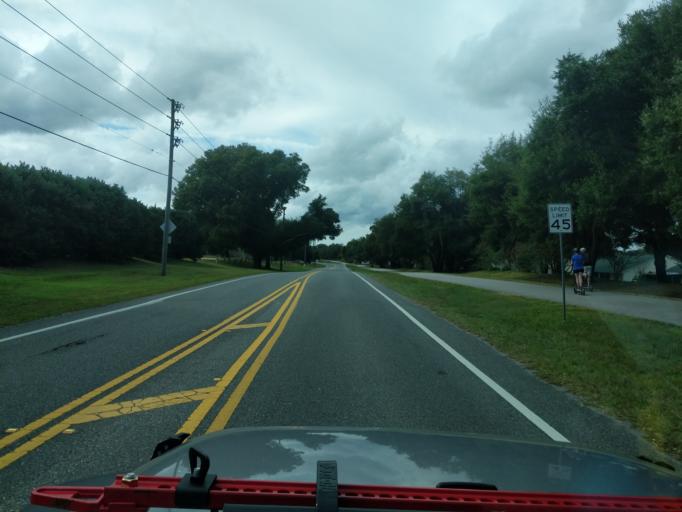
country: US
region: Florida
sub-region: Lake County
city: Clermont
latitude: 28.5687
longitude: -81.8066
